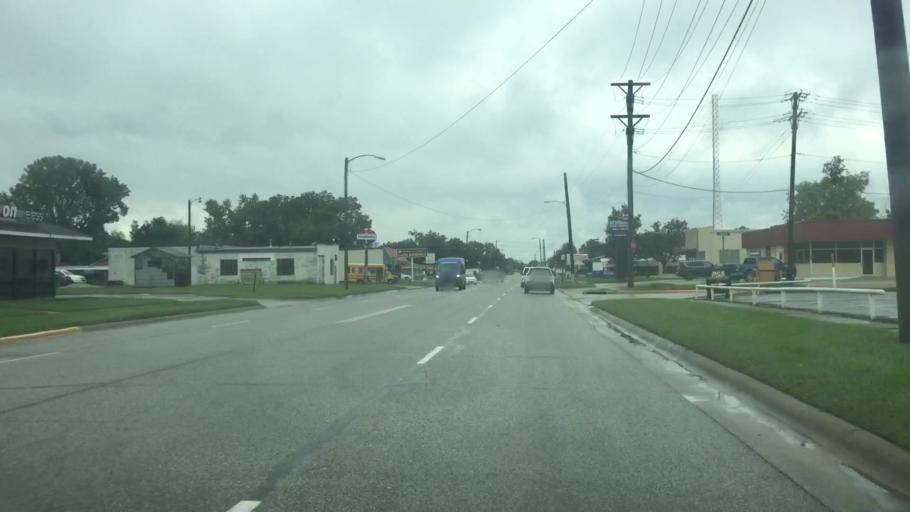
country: US
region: Kansas
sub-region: Allen County
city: Iola
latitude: 37.9287
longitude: -95.4091
